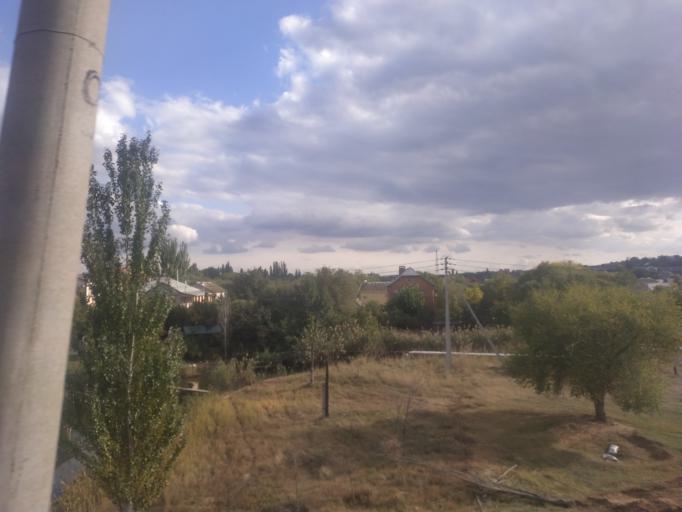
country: RU
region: Volgograd
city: Krasnoslobodsk
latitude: 48.5068
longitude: 44.5506
